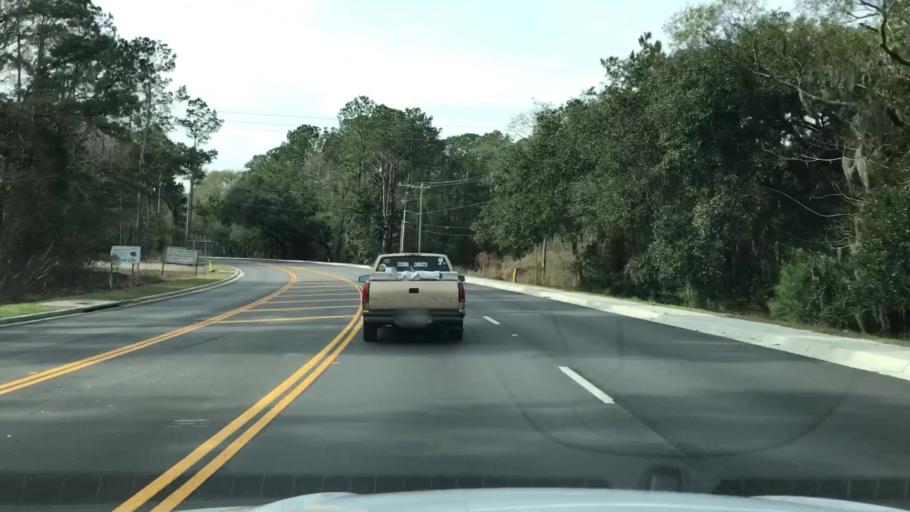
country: US
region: South Carolina
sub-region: Charleston County
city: Shell Point
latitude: 32.7515
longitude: -80.0296
